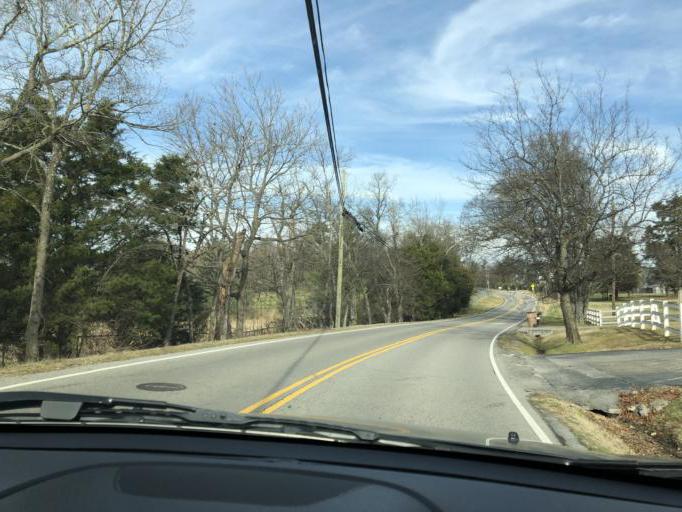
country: US
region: Tennessee
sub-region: Davidson County
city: Lakewood
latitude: 36.2193
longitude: -86.6897
